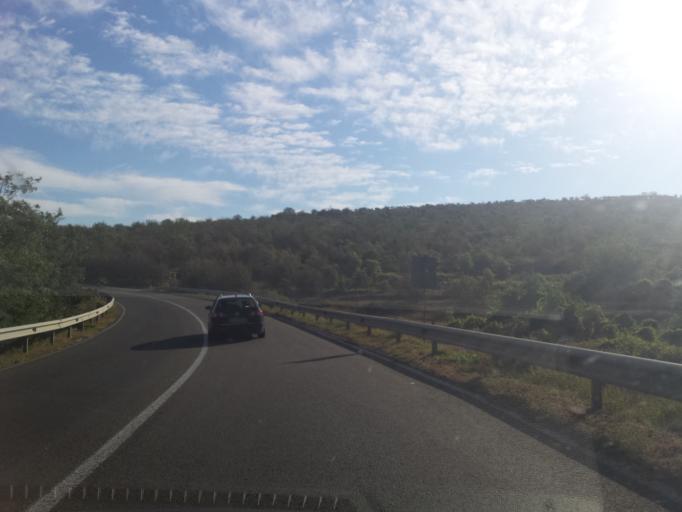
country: RO
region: Tulcea
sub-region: Municipiul Tulcea
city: Tulcea
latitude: 45.1389
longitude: 28.7747
